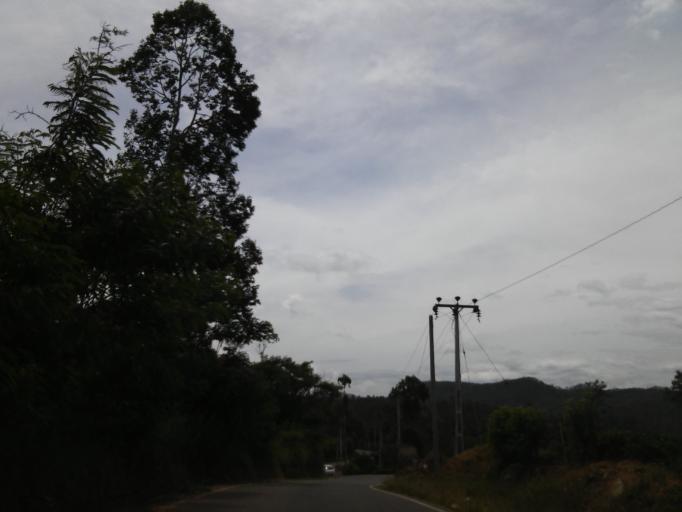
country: LK
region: Uva
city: Haputale
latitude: 6.8473
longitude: 81.0209
